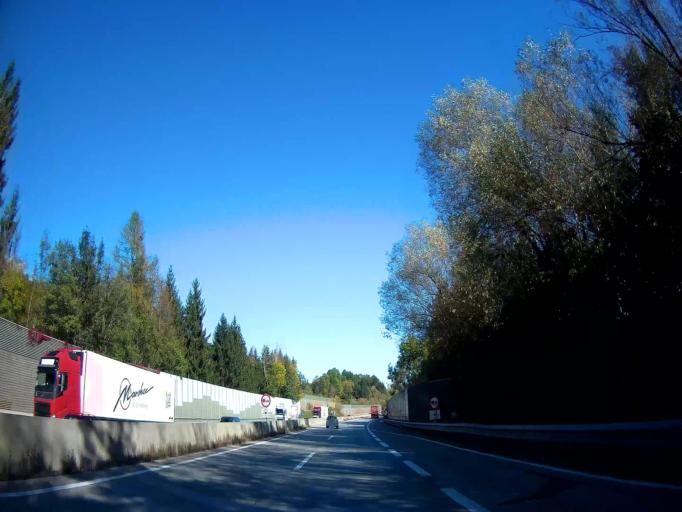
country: AT
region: Carinthia
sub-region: Politischer Bezirk Villach Land
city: Velden am Woerthersee
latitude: 46.6218
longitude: 14.0239
